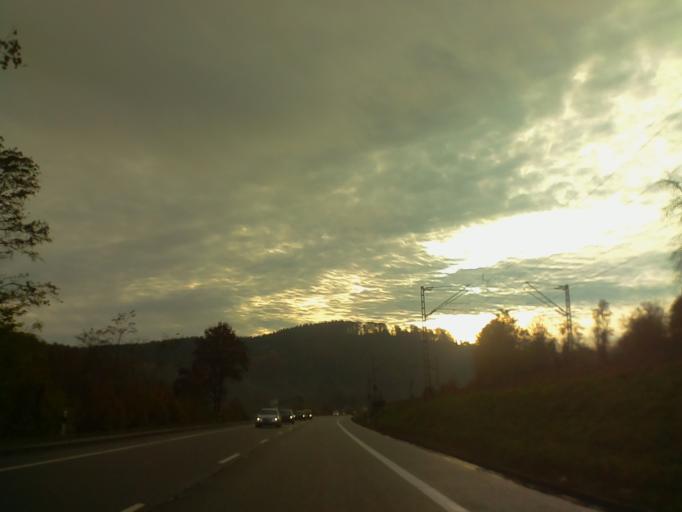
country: DE
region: Hesse
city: Neckarsteinach
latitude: 49.4034
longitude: 8.8613
